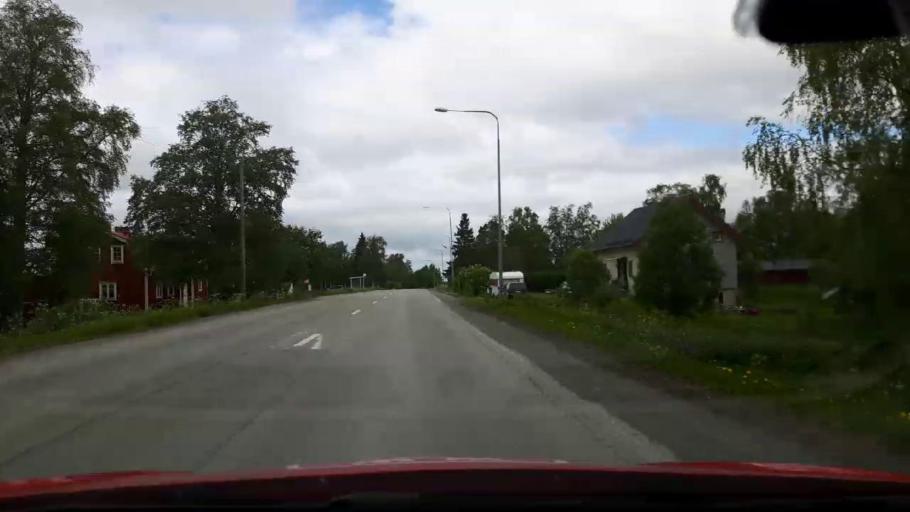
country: SE
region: Jaemtland
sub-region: Krokoms Kommun
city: Krokom
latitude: 63.3106
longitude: 14.4606
